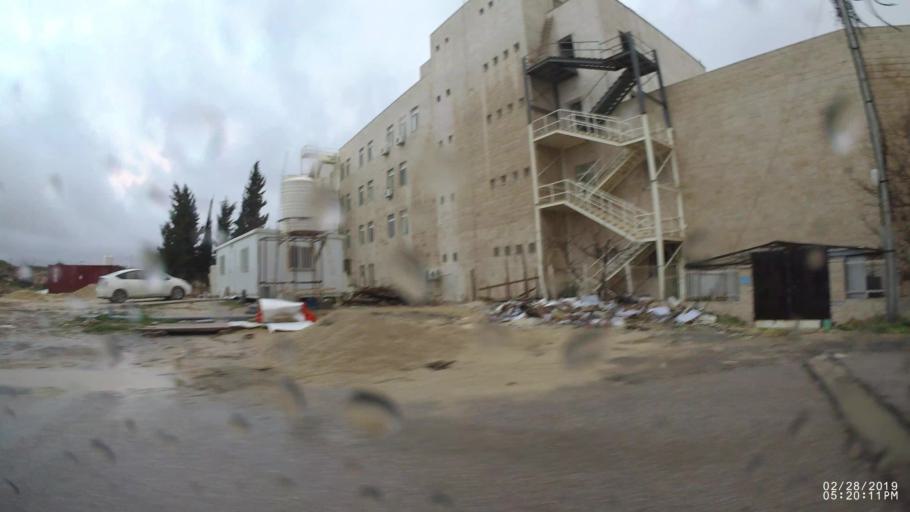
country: JO
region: Amman
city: Amman
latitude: 31.9986
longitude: 35.9200
